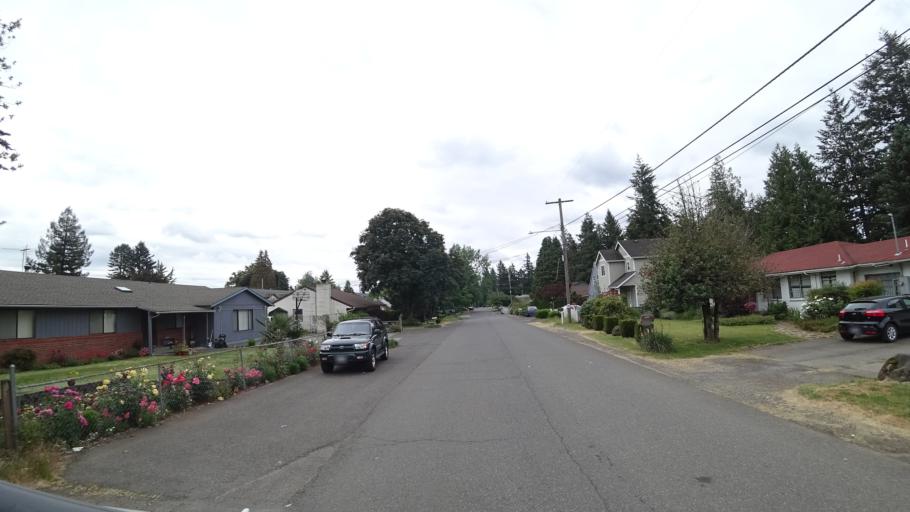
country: US
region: Oregon
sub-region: Multnomah County
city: Lents
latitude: 45.5015
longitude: -122.5409
